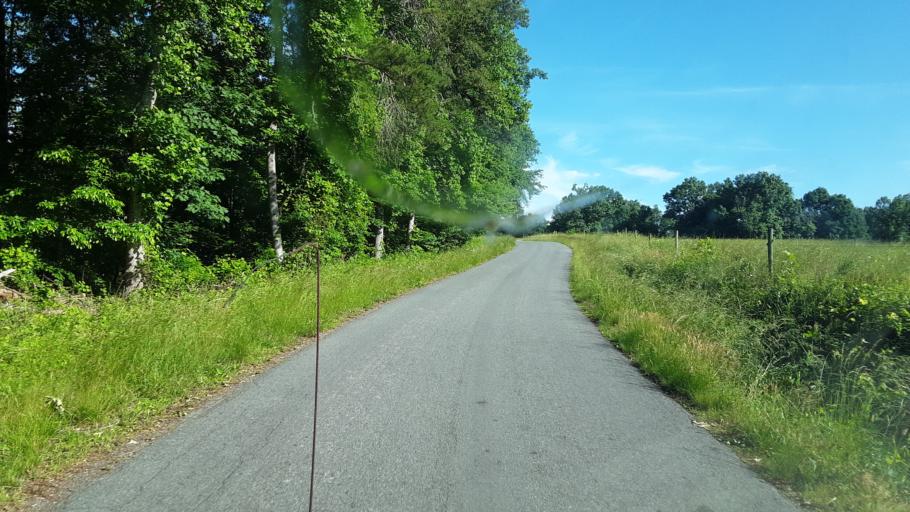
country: US
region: Virginia
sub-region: Pittsylvania County
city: Chatham
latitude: 36.8387
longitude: -79.4131
